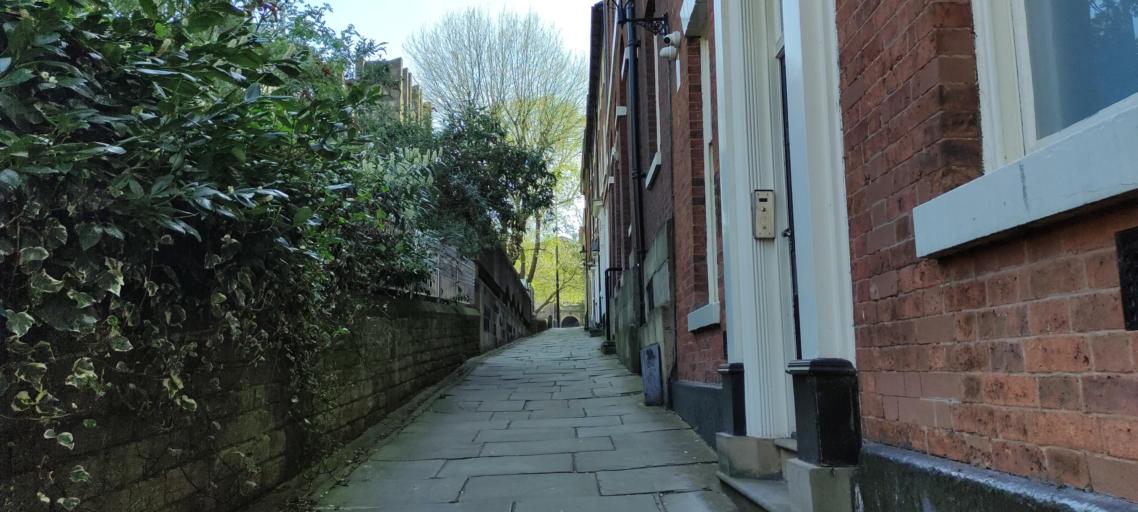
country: GB
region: England
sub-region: Sheffield
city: Sheffield
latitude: 53.3835
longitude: -1.4701
